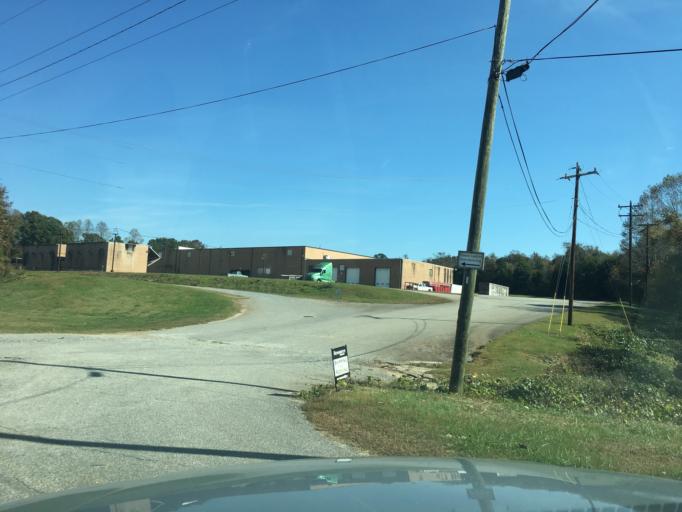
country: US
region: North Carolina
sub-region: Catawba County
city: Conover
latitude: 35.7126
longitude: -81.2446
